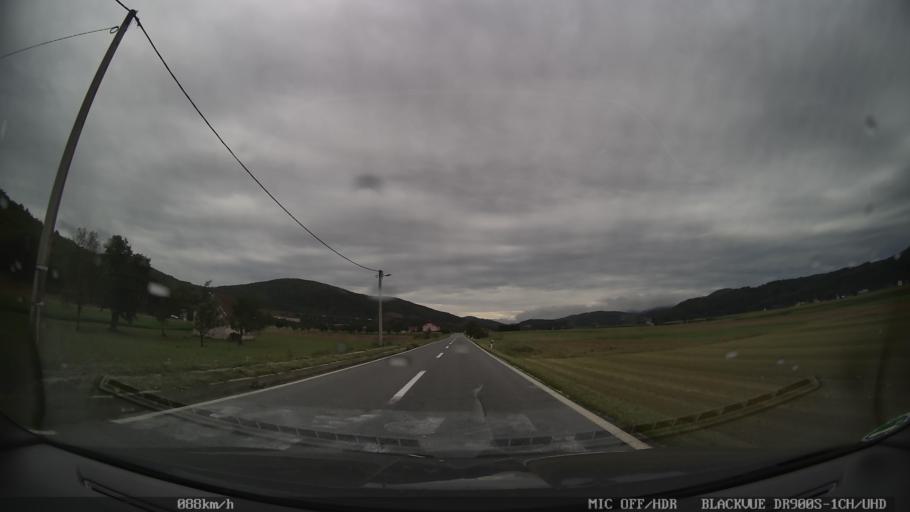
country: HR
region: Licko-Senjska
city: Otocac
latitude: 44.9123
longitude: 15.1620
